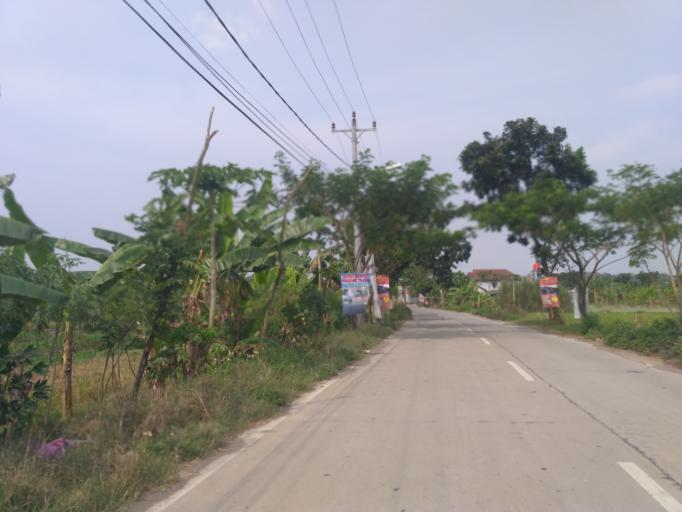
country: ID
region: Central Java
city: Mranggen
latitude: -7.0588
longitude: 110.4725
